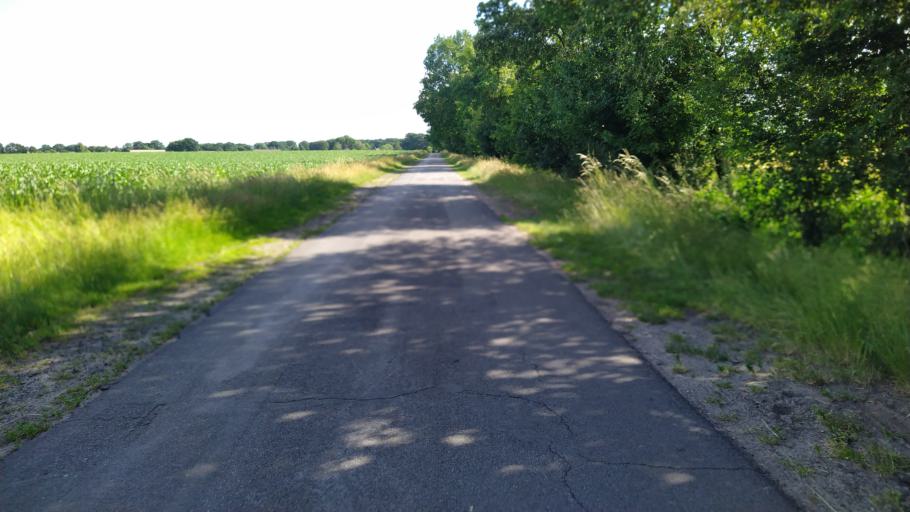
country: DE
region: Lower Saxony
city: Lintig
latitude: 53.6354
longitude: 8.8967
